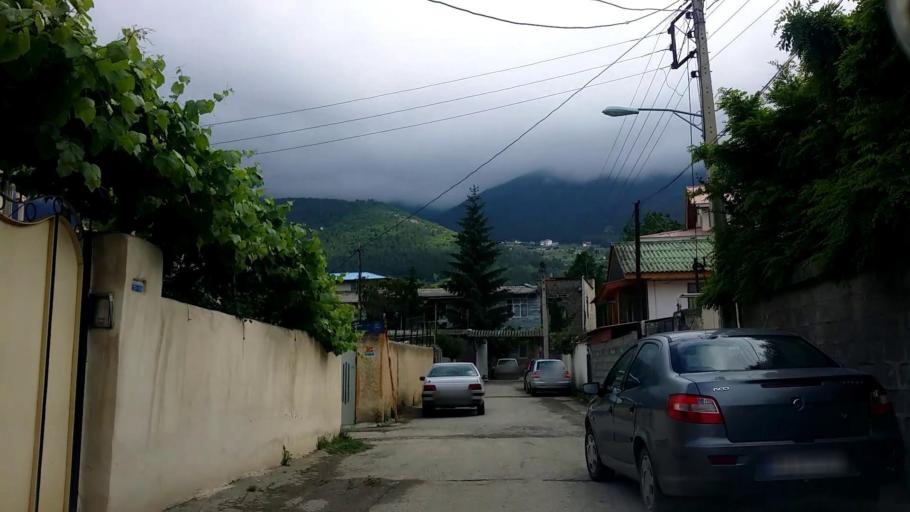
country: IR
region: Mazandaran
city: `Abbasabad
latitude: 36.5010
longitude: 51.1525
